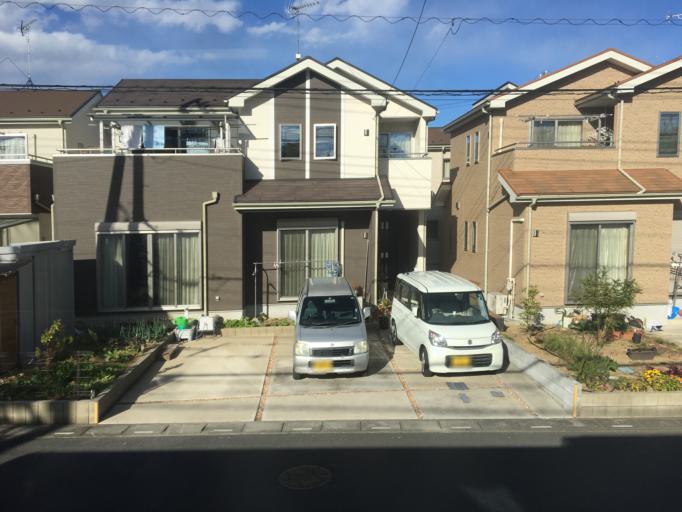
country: JP
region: Saitama
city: Ogawa
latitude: 36.0414
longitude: 139.3359
